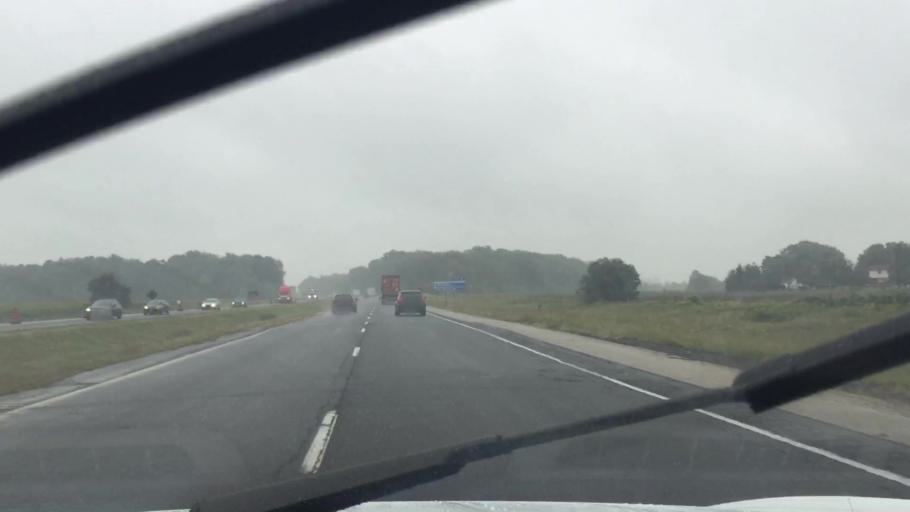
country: CA
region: Ontario
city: St. Thomas
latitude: 42.8301
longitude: -81.2965
